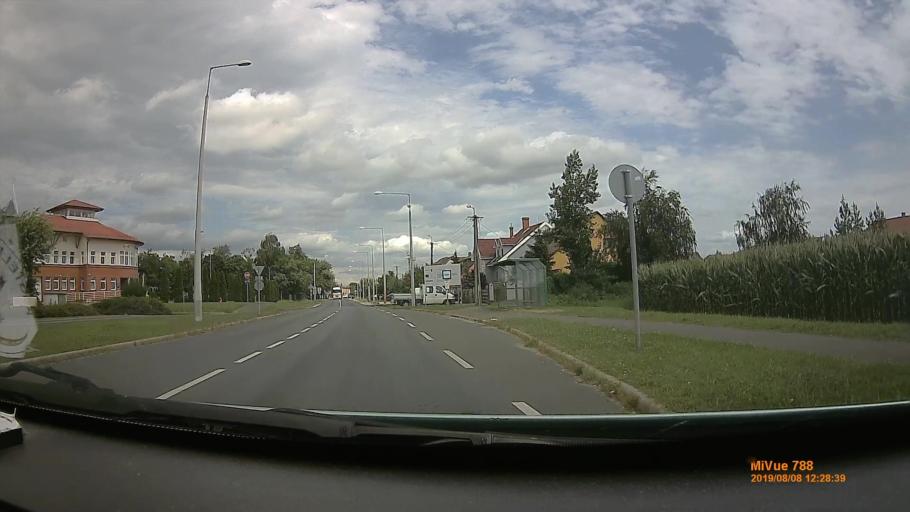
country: HU
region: Szabolcs-Szatmar-Bereg
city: Nyirbator
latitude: 47.8304
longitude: 22.1137
